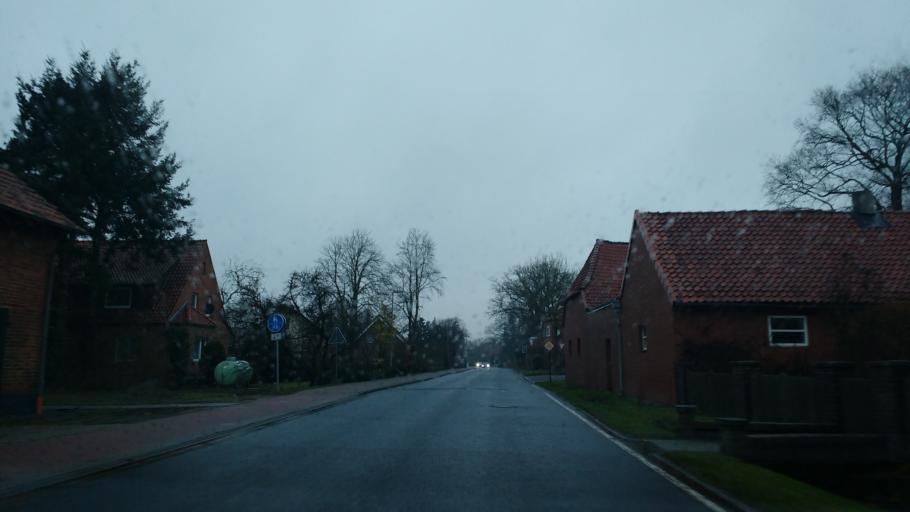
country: DE
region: Lower Saxony
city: Gilten
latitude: 52.6624
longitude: 9.5738
